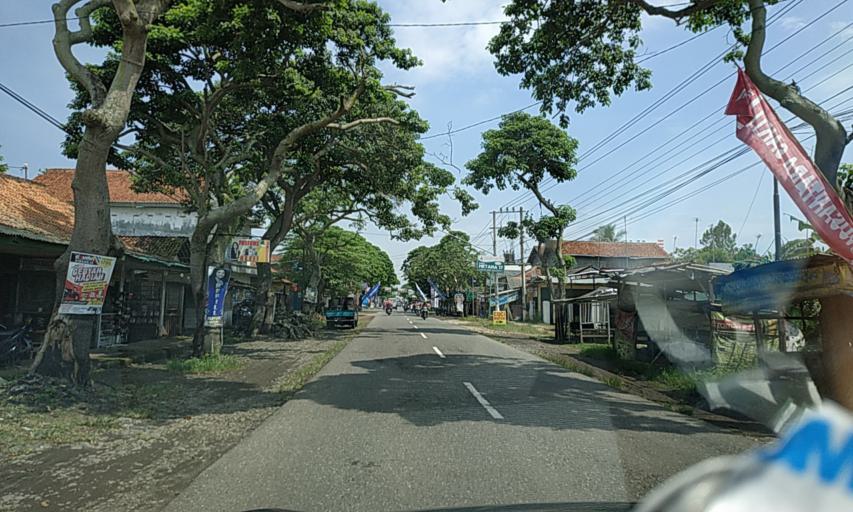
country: ID
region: Central Java
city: Gendiwu
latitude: -7.4862
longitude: 108.8105
